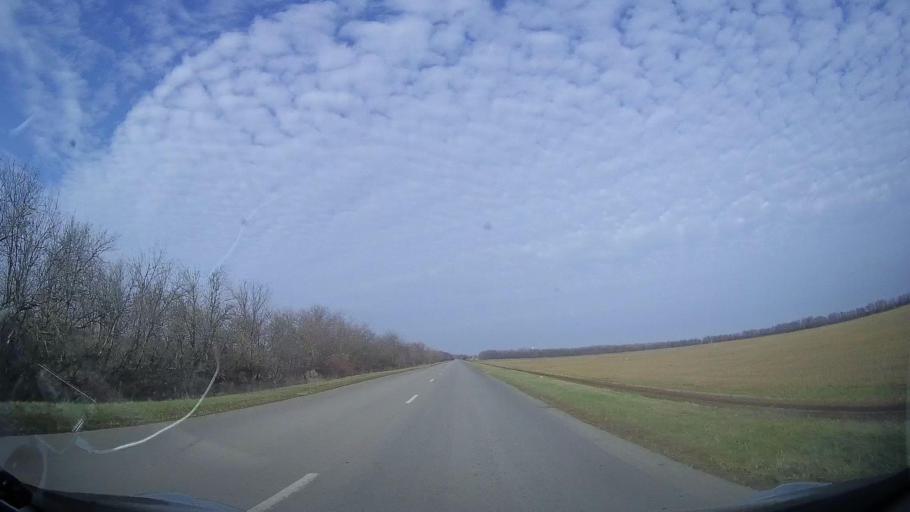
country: RU
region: Rostov
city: Gigant
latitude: 46.8256
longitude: 41.3388
